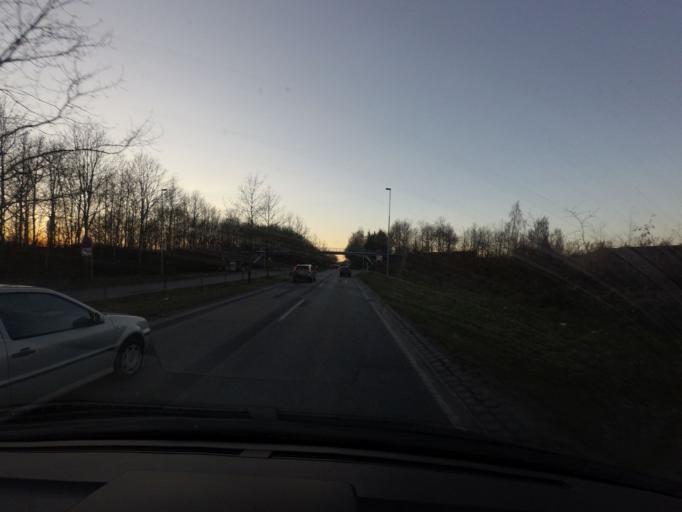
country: DK
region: South Denmark
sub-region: Odense Kommune
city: Neder Holluf
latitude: 55.3688
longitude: 10.4514
